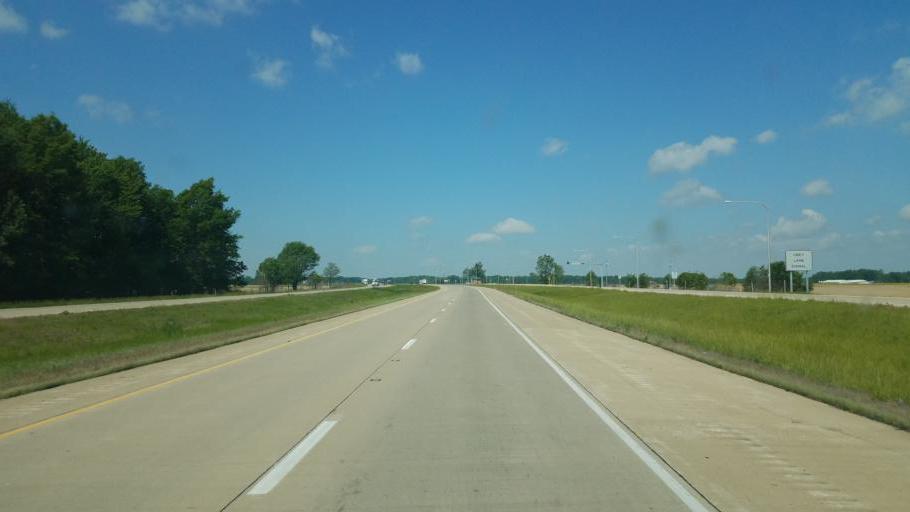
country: US
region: Illinois
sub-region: Clark County
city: Marshall
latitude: 39.4256
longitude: -87.6131
